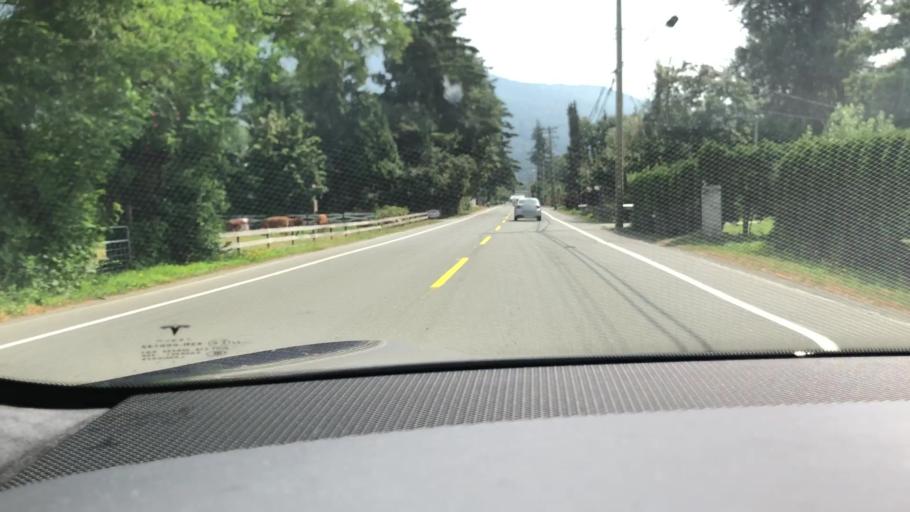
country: CA
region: British Columbia
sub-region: Fraser Valley Regional District
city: Chilliwack
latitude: 49.0871
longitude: -122.0649
